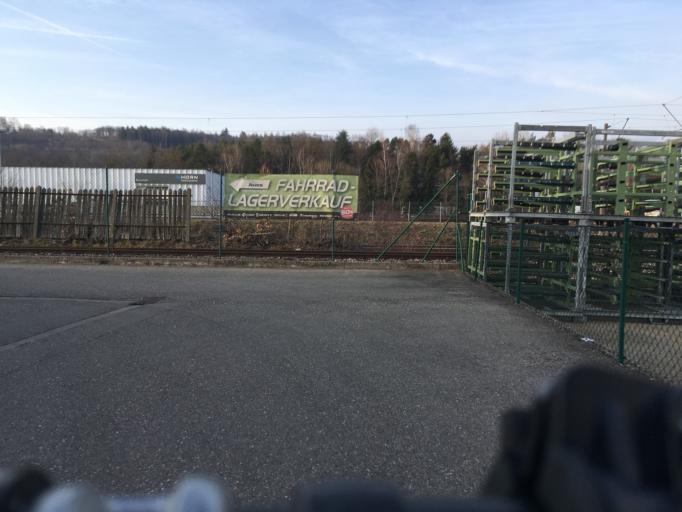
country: DE
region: Baden-Wuerttemberg
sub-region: Freiburg Region
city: Gottmadingen
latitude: 47.7395
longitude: 8.7890
